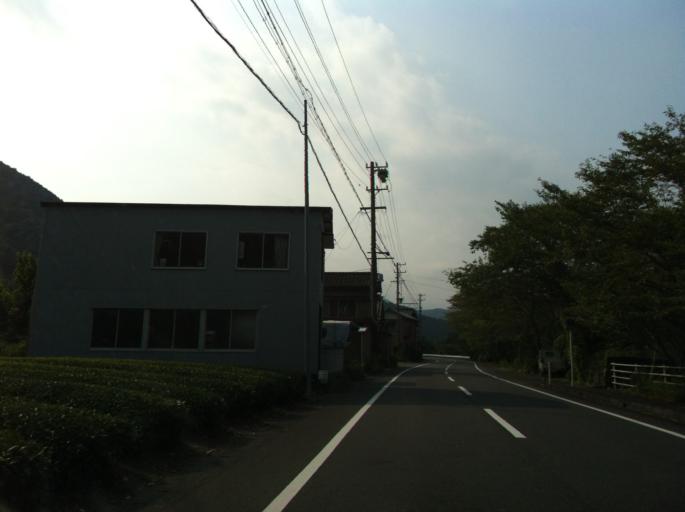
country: JP
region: Shizuoka
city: Fujieda
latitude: 34.9318
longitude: 138.2660
